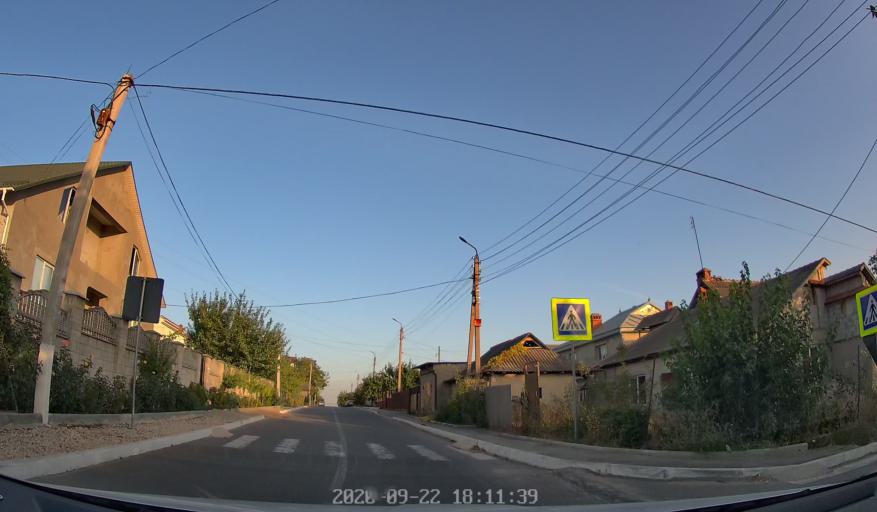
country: MD
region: Laloveni
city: Ialoveni
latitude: 46.9493
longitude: 28.7841
